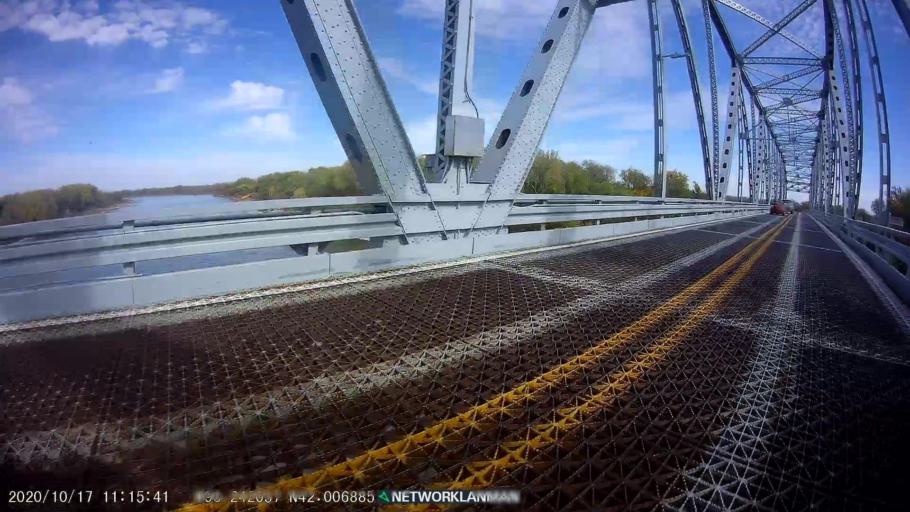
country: US
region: Iowa
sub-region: Monona County
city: Onawa
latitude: 42.0066
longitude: -96.2417
